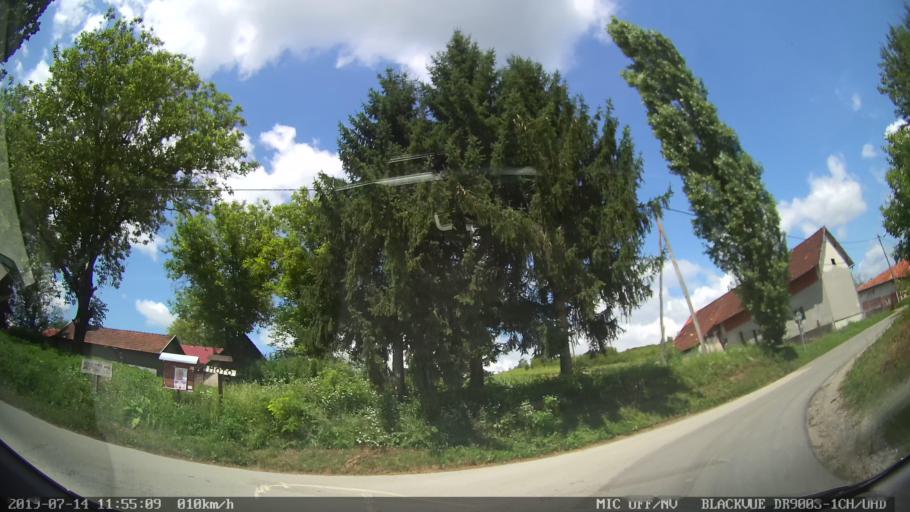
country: HR
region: Karlovacka
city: Vojnic
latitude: 45.3814
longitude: 15.6068
